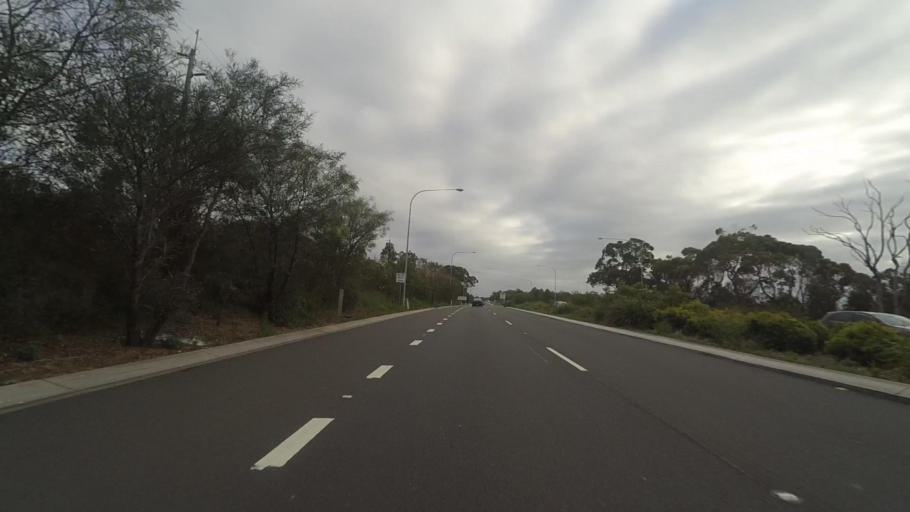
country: AU
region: New South Wales
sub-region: Sutherland Shire
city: Menai
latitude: -34.0251
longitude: 151.0076
